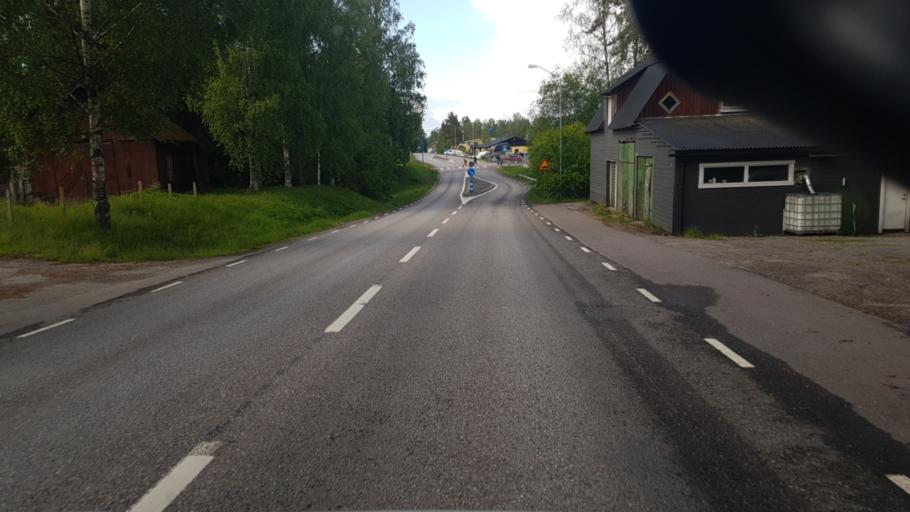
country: SE
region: Vaermland
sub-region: Eda Kommun
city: Amotfors
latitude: 59.7027
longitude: 12.1473
